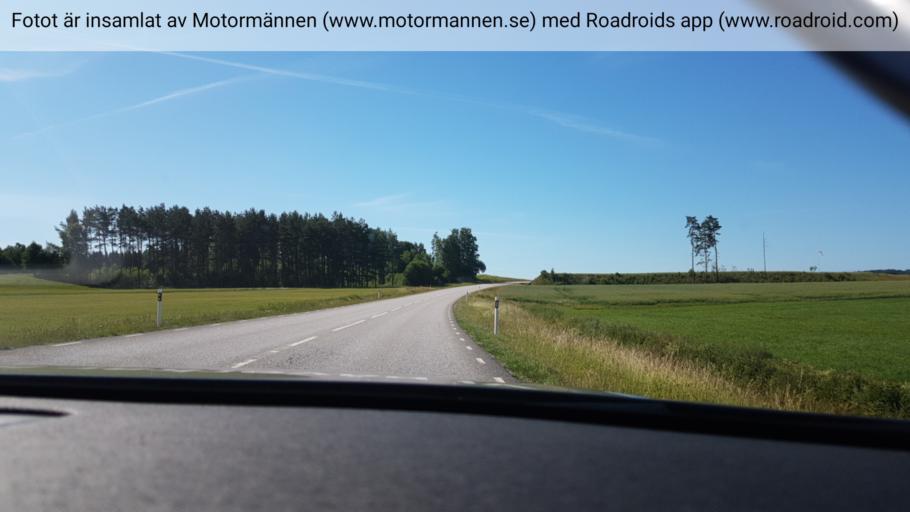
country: SE
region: Vaestra Goetaland
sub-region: Ulricehamns Kommun
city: Ulricehamn
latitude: 57.8786
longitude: 13.4344
